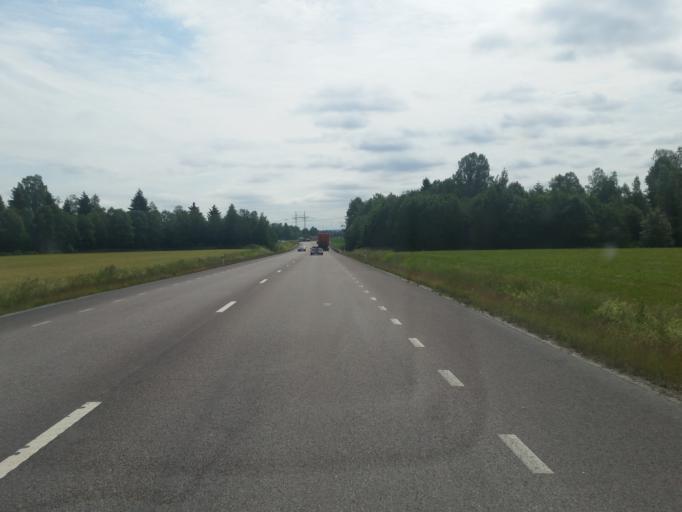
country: SE
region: Dalarna
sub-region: Gagnefs Kommun
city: Djuras
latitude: 60.5535
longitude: 15.1546
